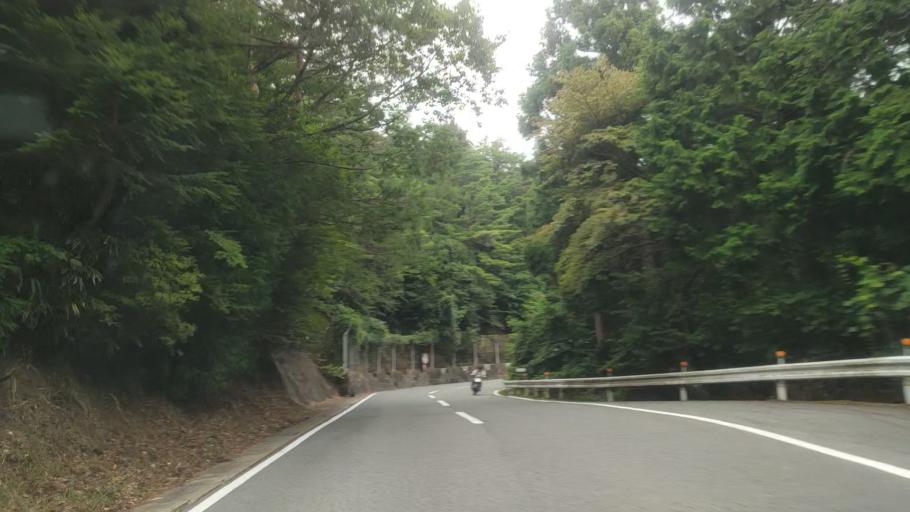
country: JP
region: Wakayama
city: Koya
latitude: 34.2214
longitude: 135.5585
